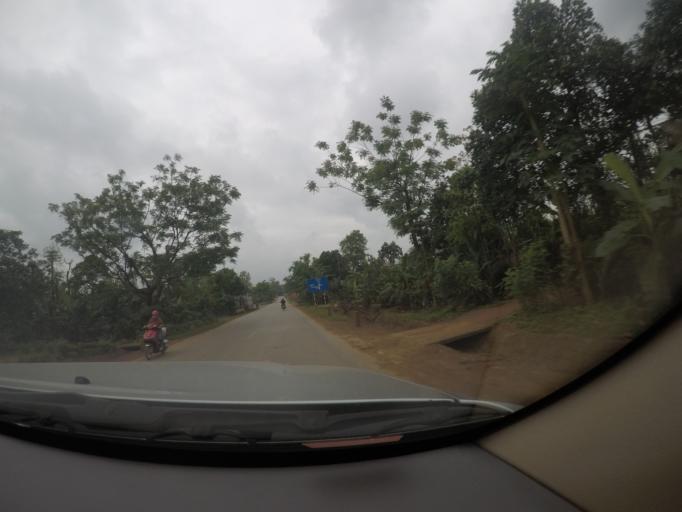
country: VN
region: Quang Tri
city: Cam Lo
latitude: 16.8868
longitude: 106.9927
